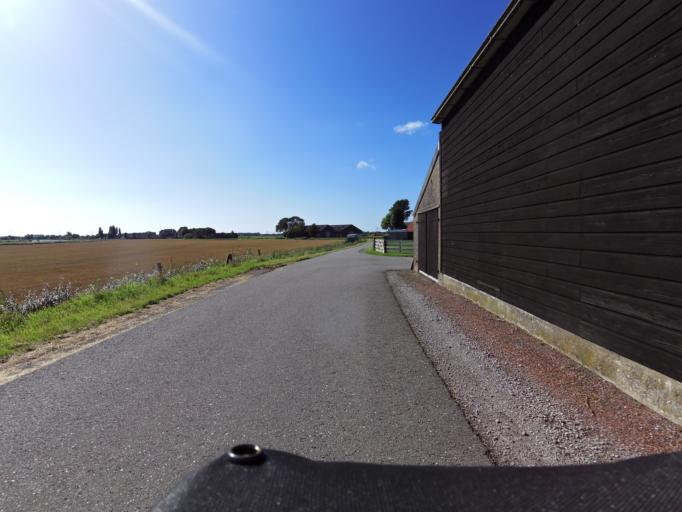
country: NL
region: South Holland
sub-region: Gemeente Spijkenisse
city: Spijkenisse
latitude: 51.8490
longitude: 4.2876
